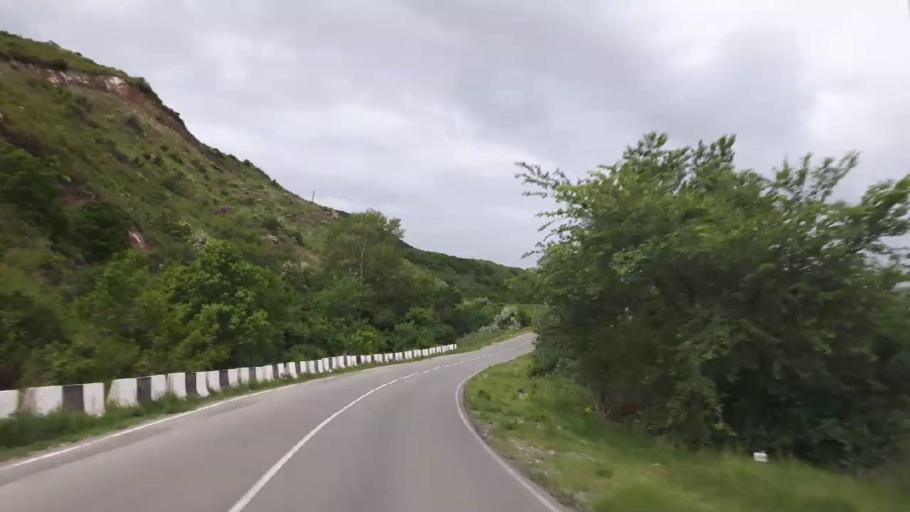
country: GE
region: Shida Kartli
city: Gori
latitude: 41.9919
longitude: 44.0343
